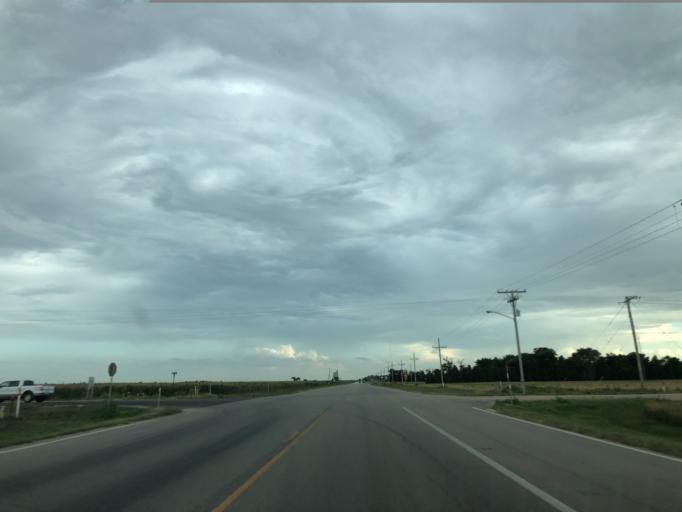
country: US
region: Kansas
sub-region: Rice County
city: Lyons
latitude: 38.2905
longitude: -98.2020
